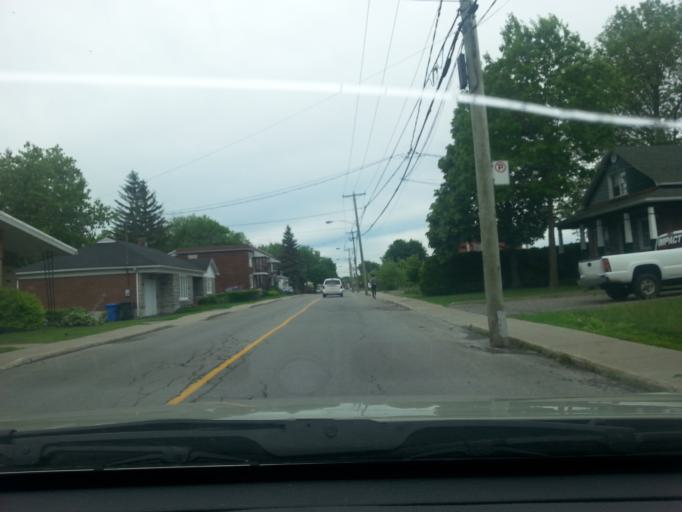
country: CA
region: Quebec
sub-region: Lanaudiere
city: Terrebonne
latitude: 45.6953
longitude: -73.6242
